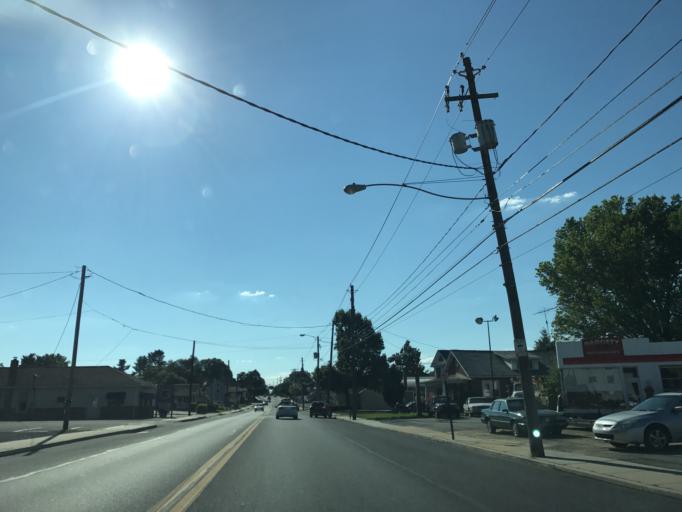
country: US
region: Pennsylvania
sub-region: Lancaster County
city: Mount Joy
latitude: 40.1121
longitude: -76.5129
